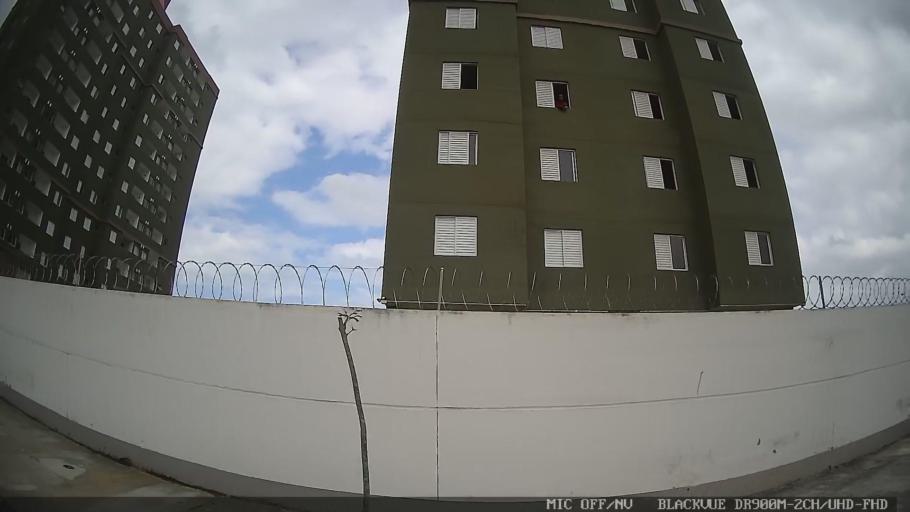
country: BR
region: Sao Paulo
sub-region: Guaruja
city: Guaruja
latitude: -23.9877
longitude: -46.2807
